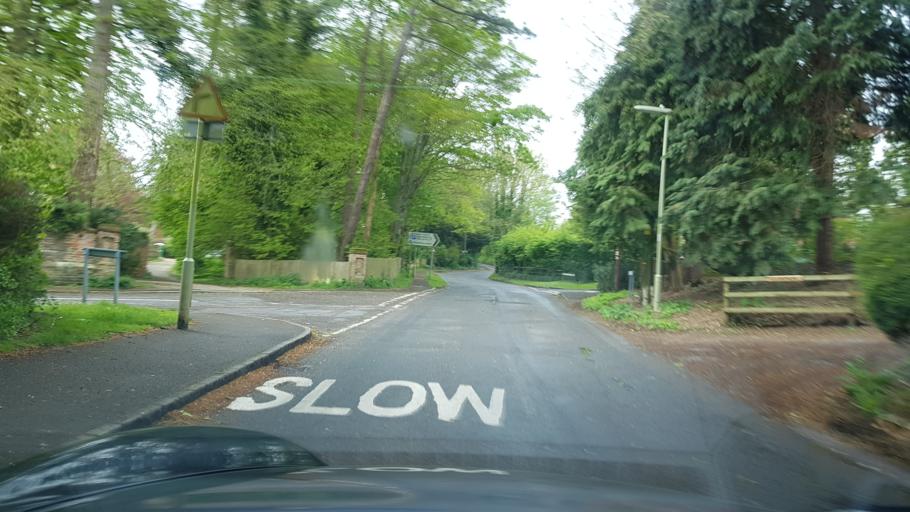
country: GB
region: England
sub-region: Hampshire
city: Kingsclere
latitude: 51.3255
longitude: -1.2510
